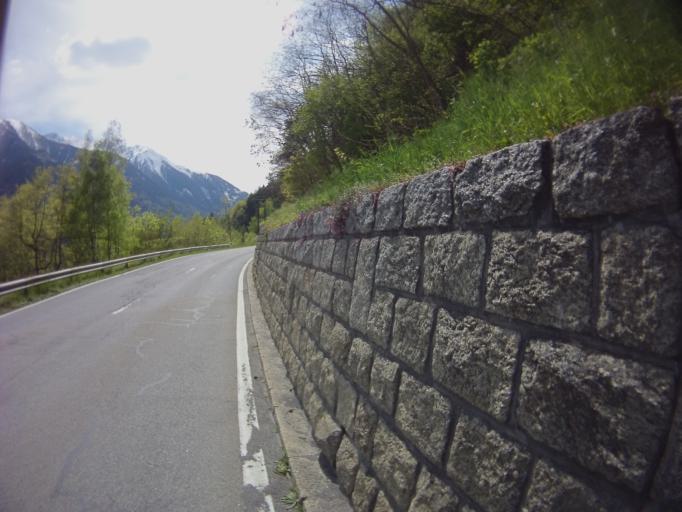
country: CH
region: Valais
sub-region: Martigny District
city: Martigny-Combe
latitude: 46.0862
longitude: 7.0422
